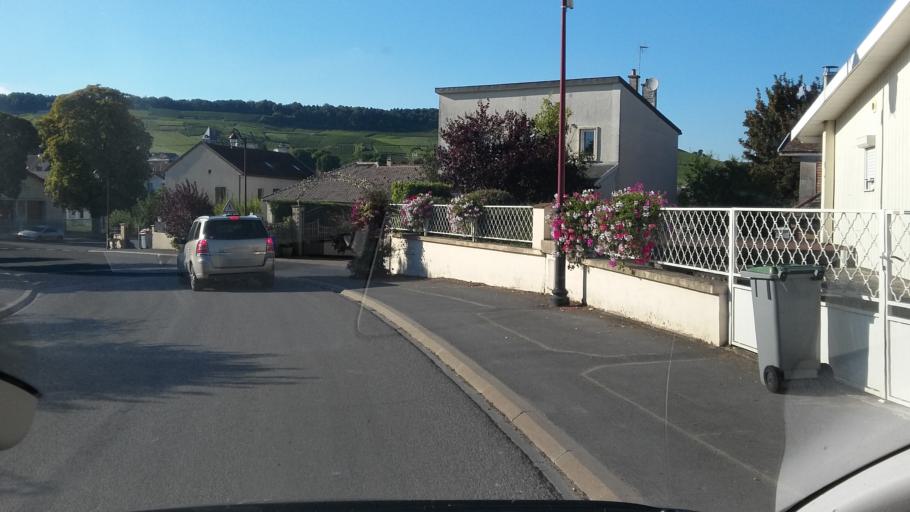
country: FR
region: Champagne-Ardenne
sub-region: Departement de la Marne
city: Le Mesnil-sur-Oger
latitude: 48.9575
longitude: 4.0158
